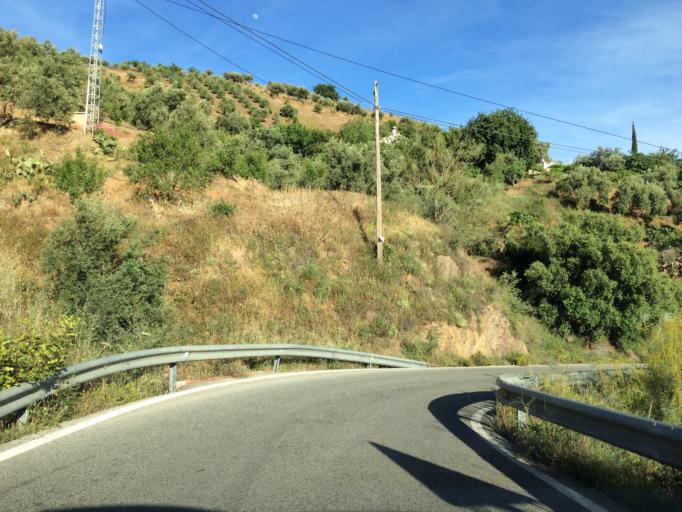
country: ES
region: Andalusia
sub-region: Provincia de Malaga
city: Totalan
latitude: 36.7480
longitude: -4.3306
